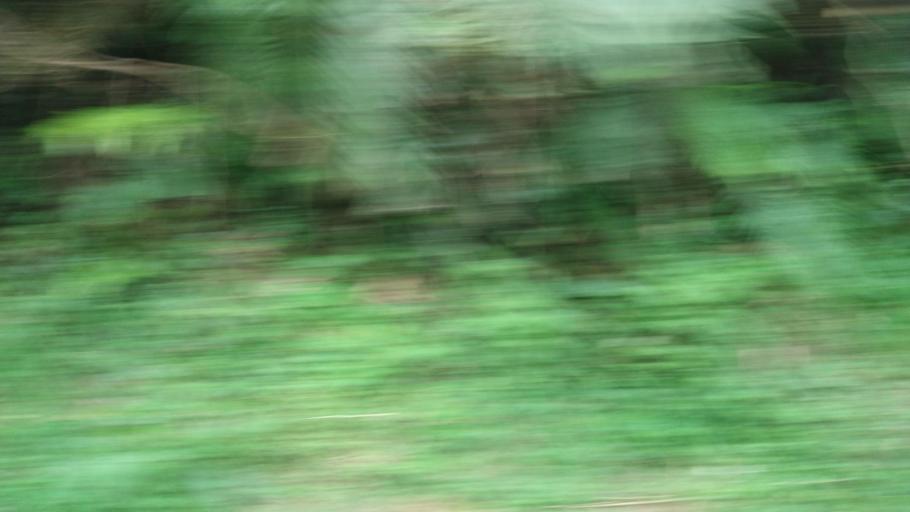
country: TW
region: Taiwan
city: Daxi
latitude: 24.9110
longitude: 121.3998
